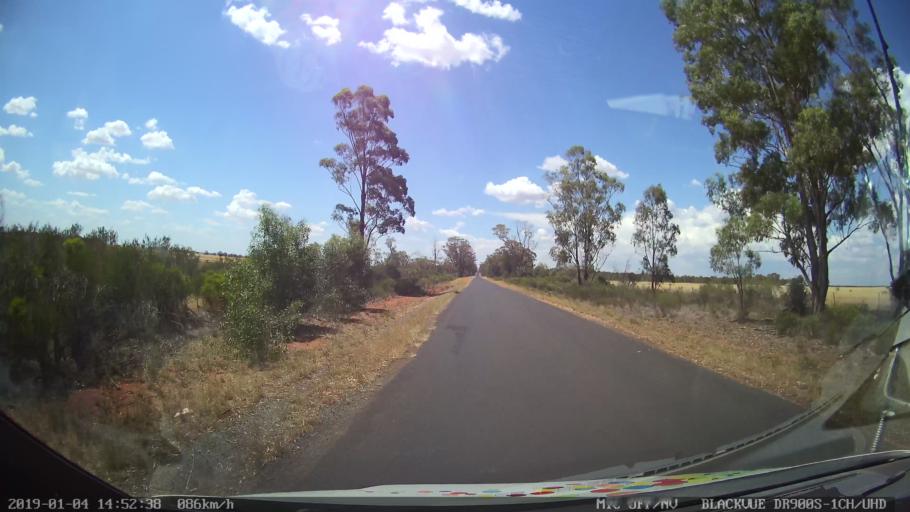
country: AU
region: New South Wales
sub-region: Dubbo Municipality
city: Dubbo
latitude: -32.0134
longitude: 148.6502
